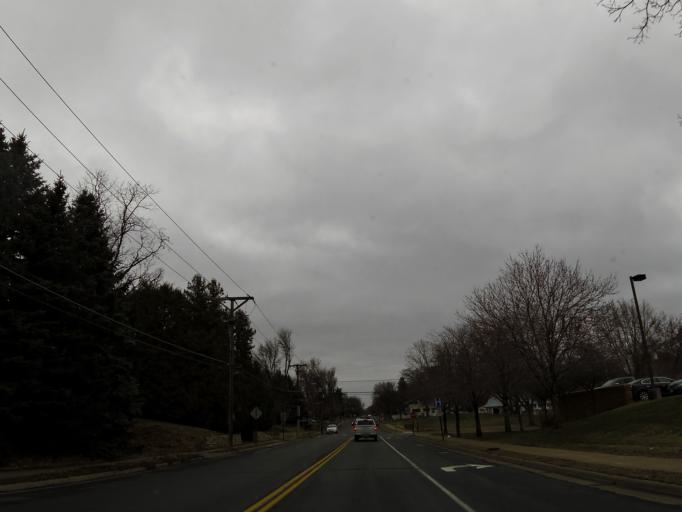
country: US
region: Minnesota
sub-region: Washington County
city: Stillwater
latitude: 45.0475
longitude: -92.8192
